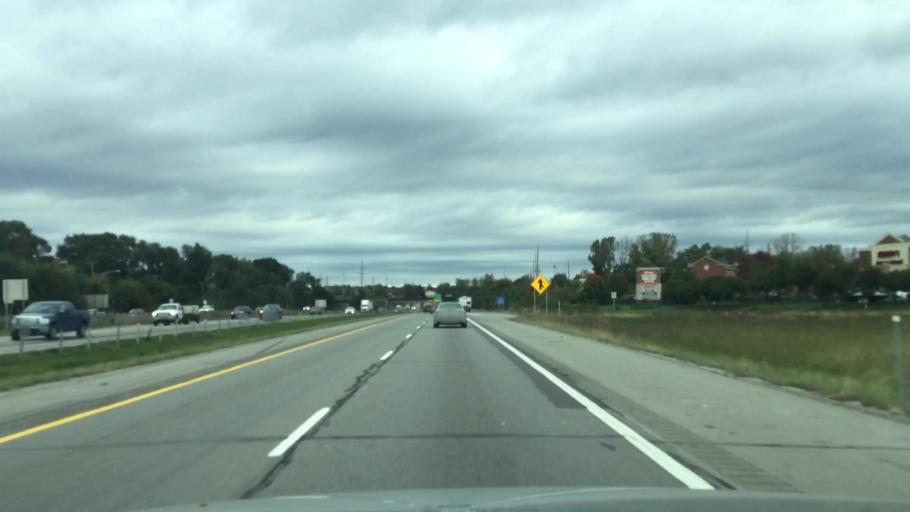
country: US
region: Michigan
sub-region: Livingston County
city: Brighton
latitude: 42.5072
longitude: -83.7580
